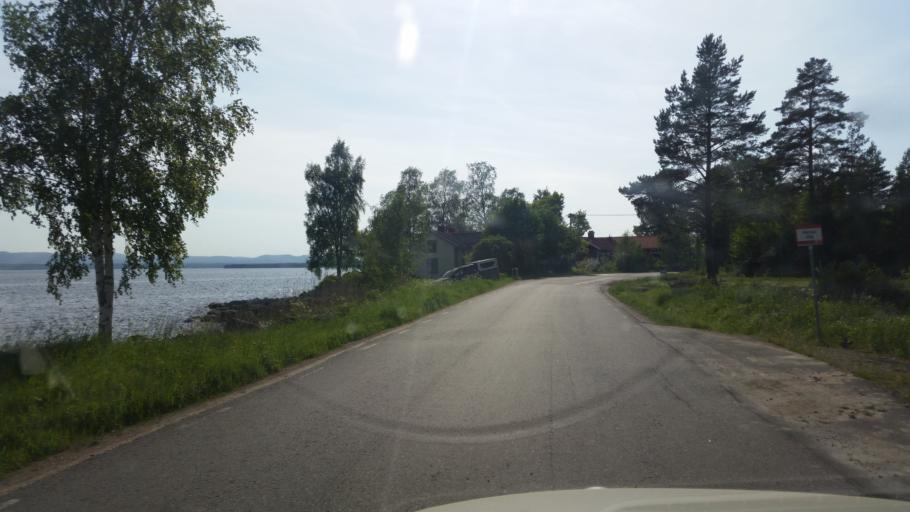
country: SE
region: Gaevleborg
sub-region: Hudiksvalls Kommun
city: Delsbo
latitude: 61.8286
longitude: 16.7475
